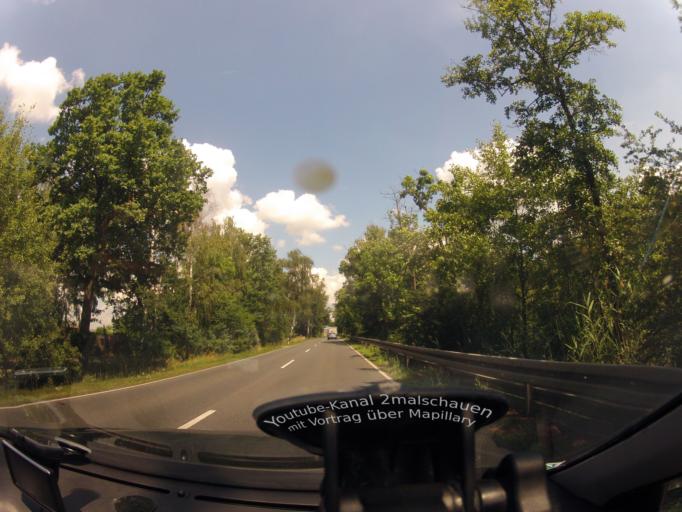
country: DE
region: Saxony
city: Zinna
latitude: 51.5483
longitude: 12.9592
